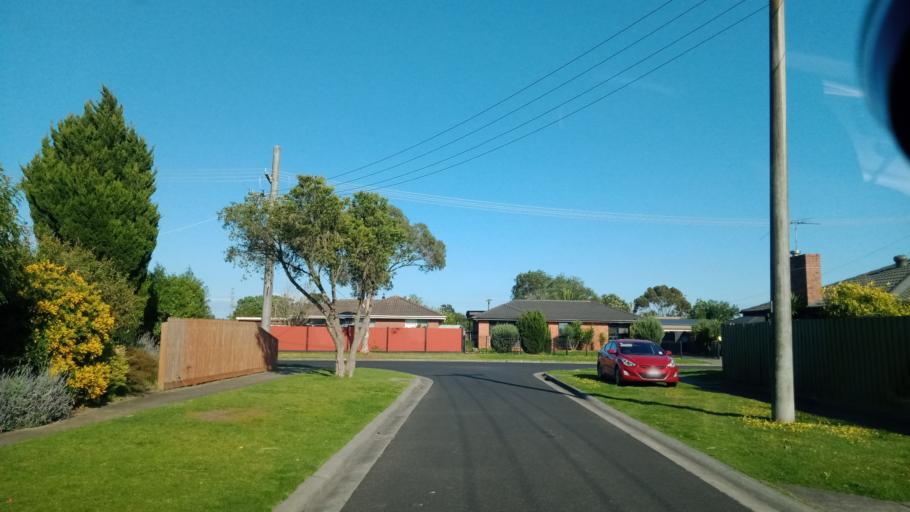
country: AU
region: Victoria
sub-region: Casey
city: Cranbourne West
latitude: -38.0924
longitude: 145.2721
